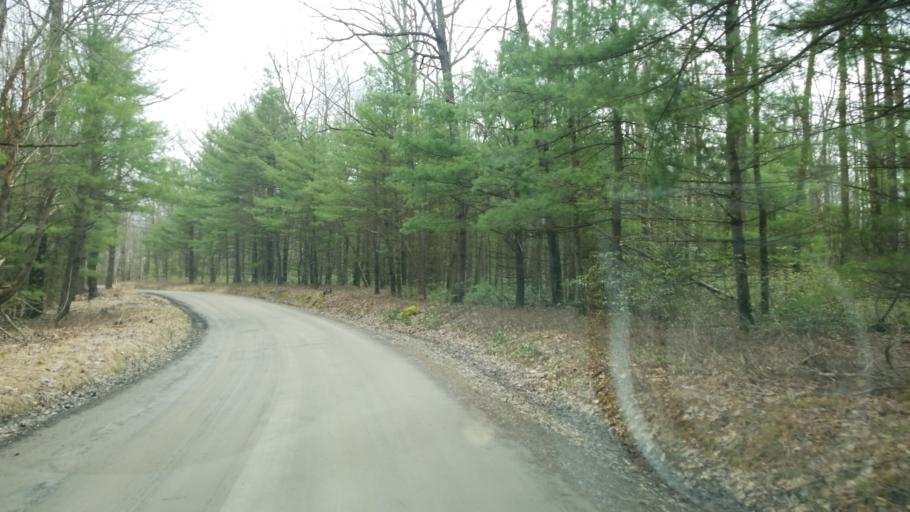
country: US
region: Pennsylvania
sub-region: Clearfield County
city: Shiloh
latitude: 41.1655
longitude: -78.2530
